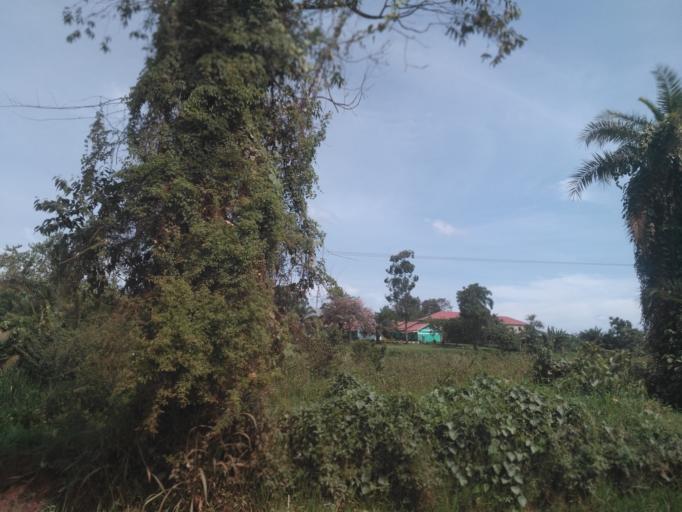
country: UG
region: Central Region
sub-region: Wakiso District
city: Kireka
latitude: 0.4410
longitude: 32.5926
